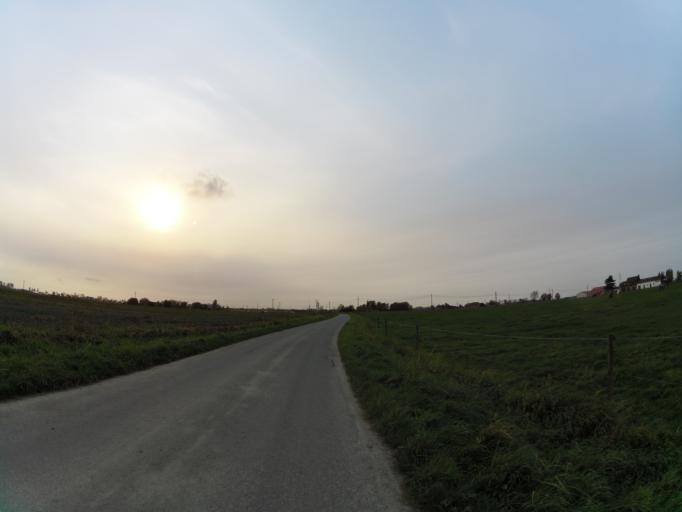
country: BE
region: Flanders
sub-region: Provincie West-Vlaanderen
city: Oudenburg
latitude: 51.2198
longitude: 3.0242
